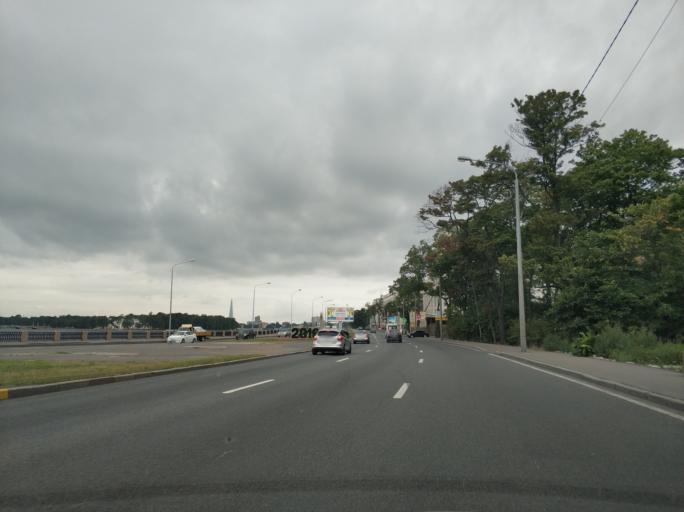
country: RU
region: St.-Petersburg
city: Petrogradka
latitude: 59.9804
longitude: 30.3212
